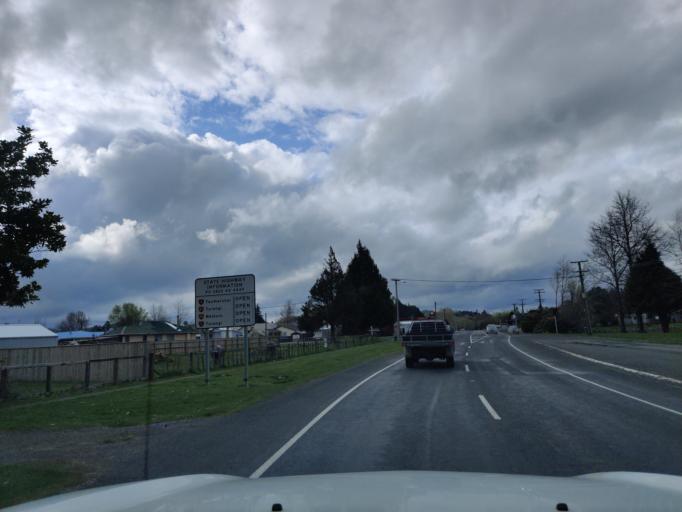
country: NZ
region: Manawatu-Wanganui
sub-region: Ruapehu District
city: Waiouru
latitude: -39.4297
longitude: 175.2818
